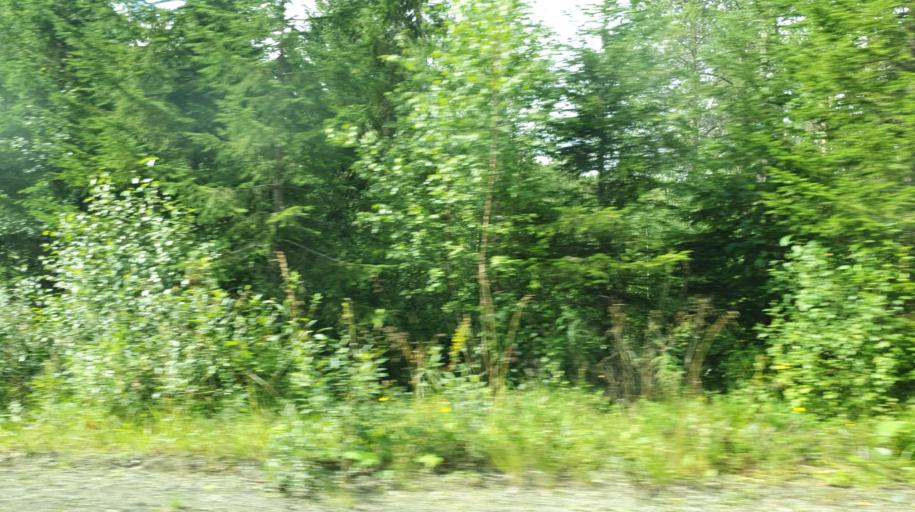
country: NO
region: Nord-Trondelag
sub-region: Levanger
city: Skogn
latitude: 63.5928
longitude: 11.2600
